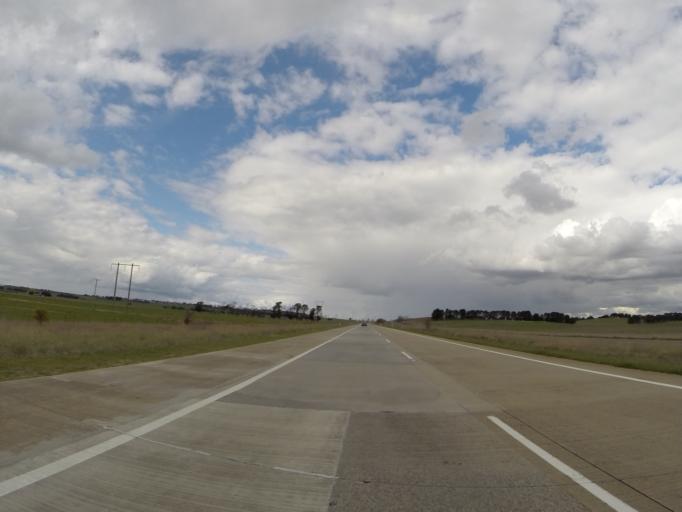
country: AU
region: New South Wales
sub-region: Goulburn Mulwaree
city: Goulburn
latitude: -34.8071
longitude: 149.5530
